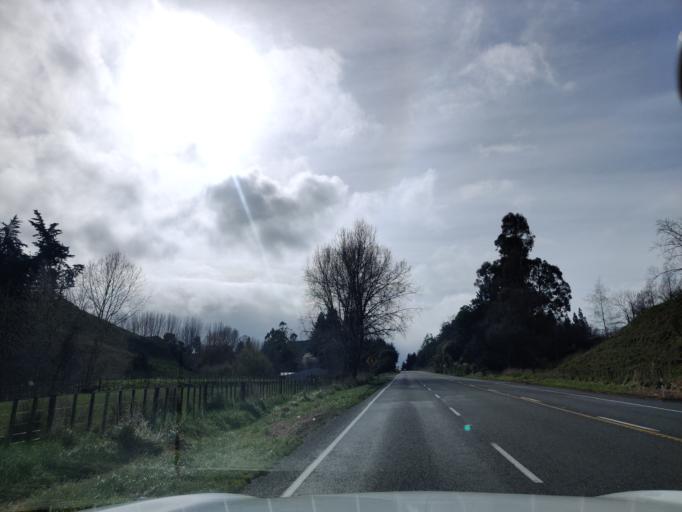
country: NZ
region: Manawatu-Wanganui
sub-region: Ruapehu District
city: Waiouru
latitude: -39.7737
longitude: 175.7922
